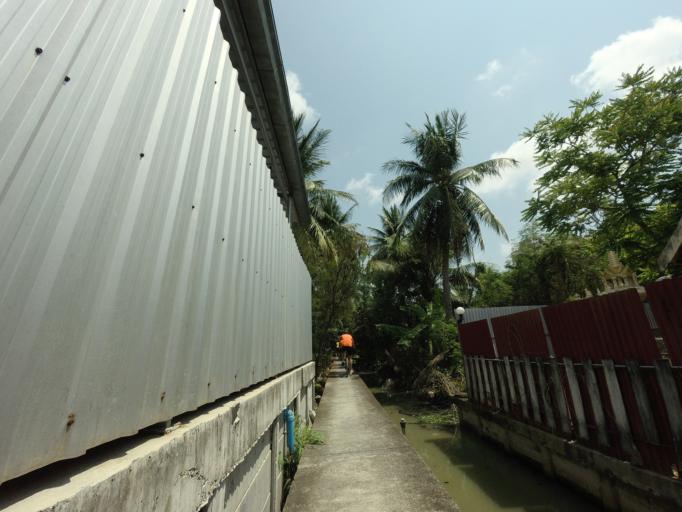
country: TH
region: Bangkok
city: Chom Thong
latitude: 13.6538
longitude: 100.4849
